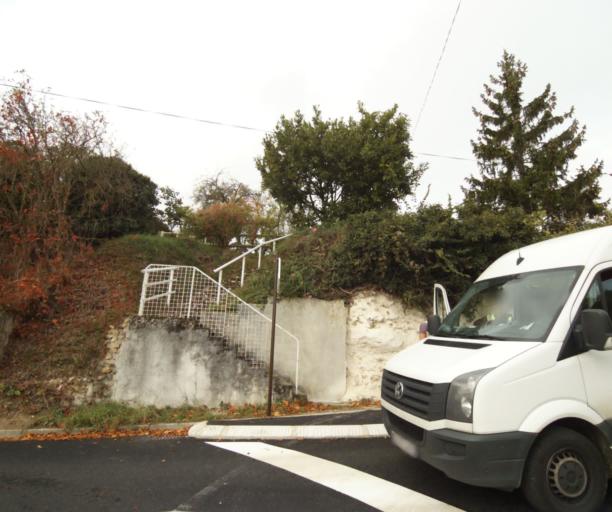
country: FR
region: Centre
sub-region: Departement d'Eure-et-Loir
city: Dreux
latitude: 48.7418
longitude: 1.3706
